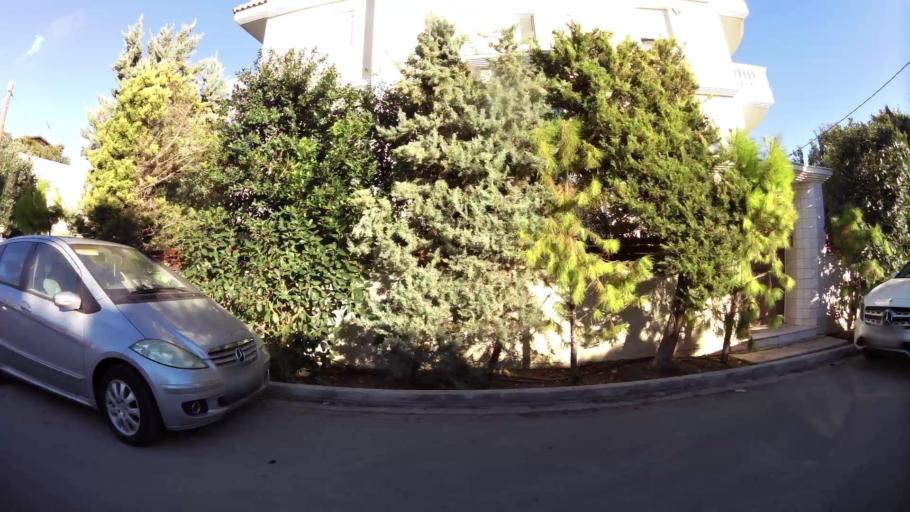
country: GR
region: Attica
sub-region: Nomarchia Anatolikis Attikis
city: Vari
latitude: 37.8256
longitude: 23.8065
